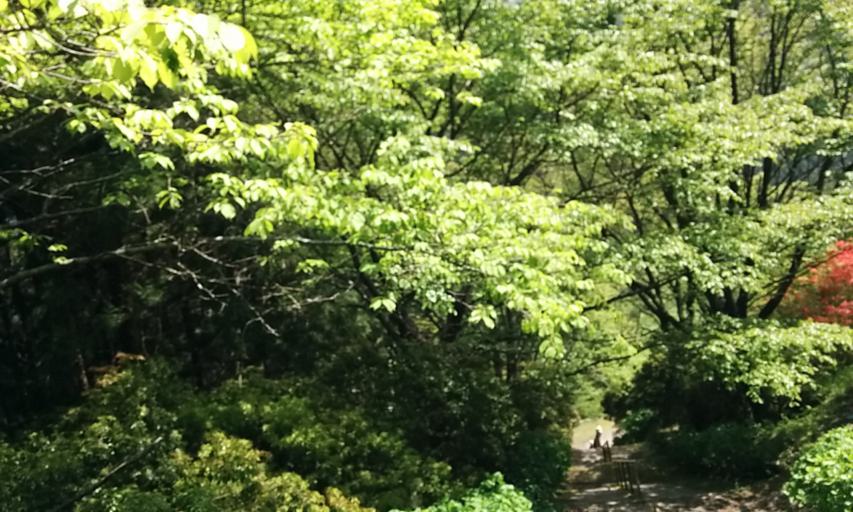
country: JP
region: Ehime
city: Niihama
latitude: 33.8776
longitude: 133.3137
